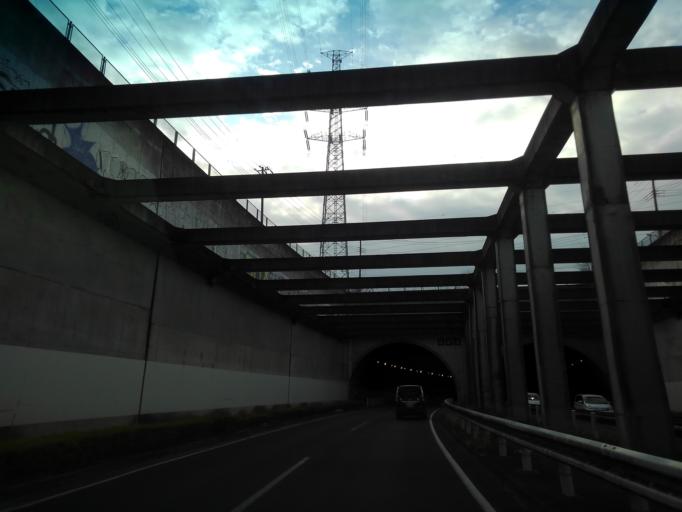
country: JP
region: Tokyo
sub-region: Machida-shi
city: Machida
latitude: 35.5934
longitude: 139.4501
